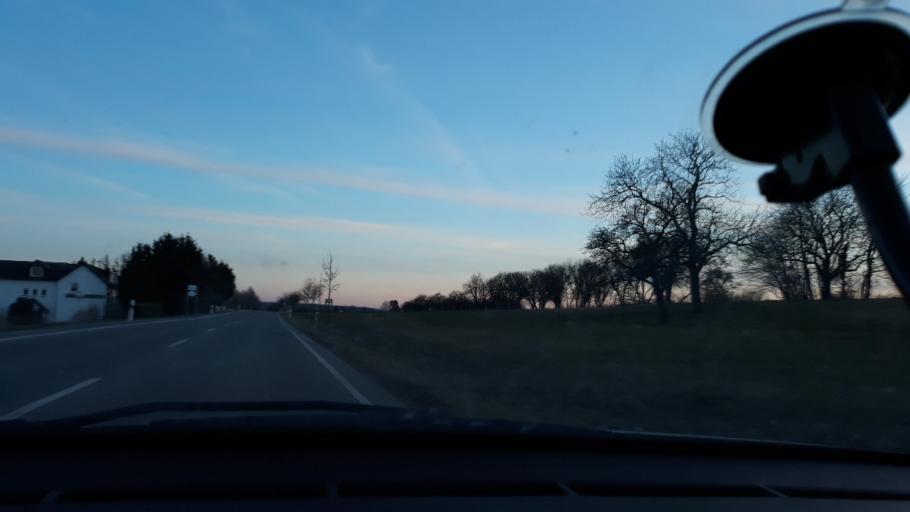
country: DE
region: Saarland
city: Blieskastel
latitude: 49.2251
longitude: 7.1833
